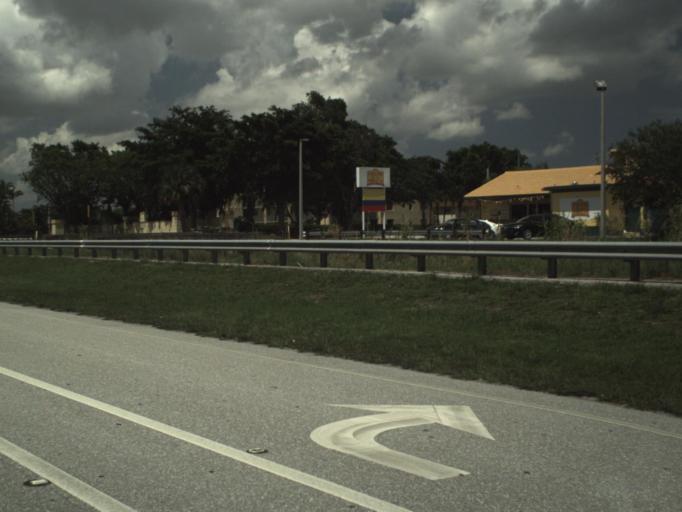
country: US
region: Florida
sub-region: Broward County
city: Parkland
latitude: 26.3351
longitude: -80.2030
